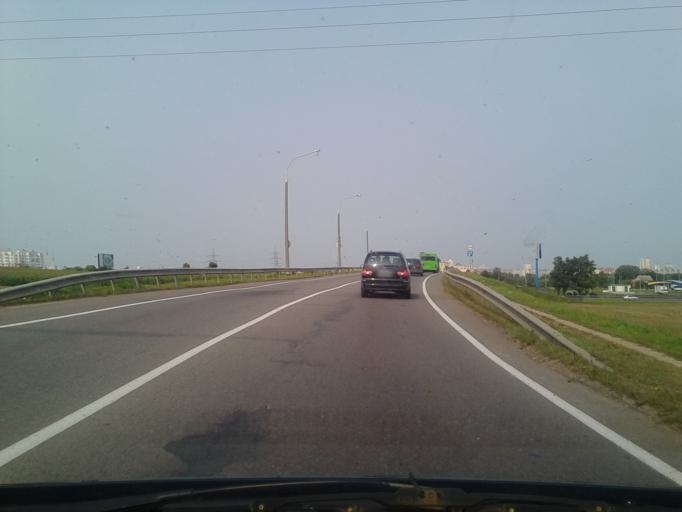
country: BY
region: Minsk
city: Machulishchy
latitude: 53.8313
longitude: 27.6009
